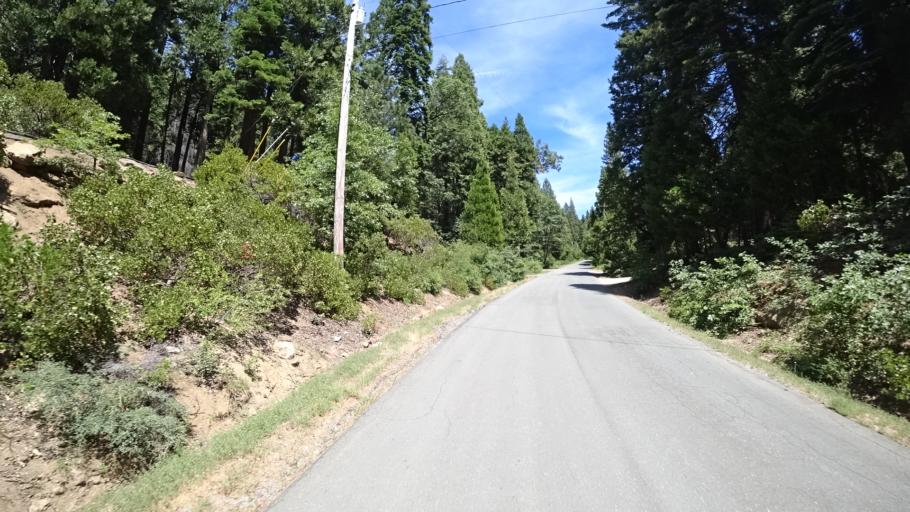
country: US
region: California
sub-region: Calaveras County
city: Arnold
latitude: 38.3084
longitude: -120.2746
